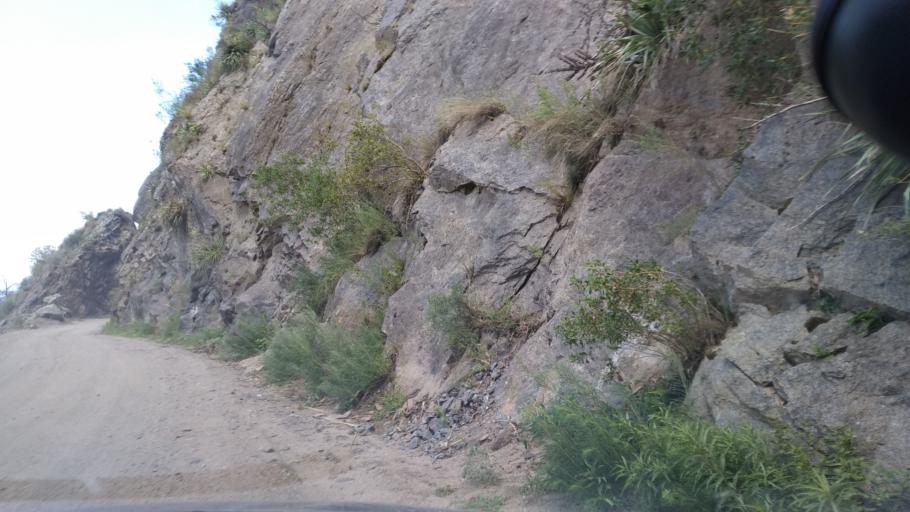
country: AR
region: Cordoba
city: Salsacate
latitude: -31.3759
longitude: -65.3940
